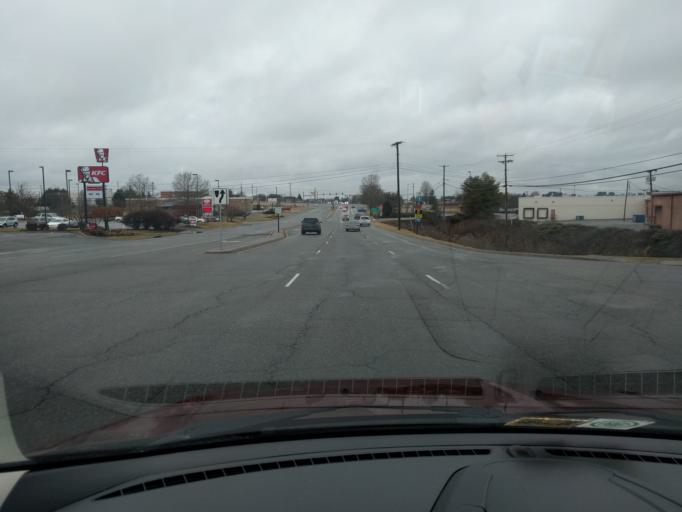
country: US
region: Virginia
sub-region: Montgomery County
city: Merrimac
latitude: 37.1642
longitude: -80.4199
